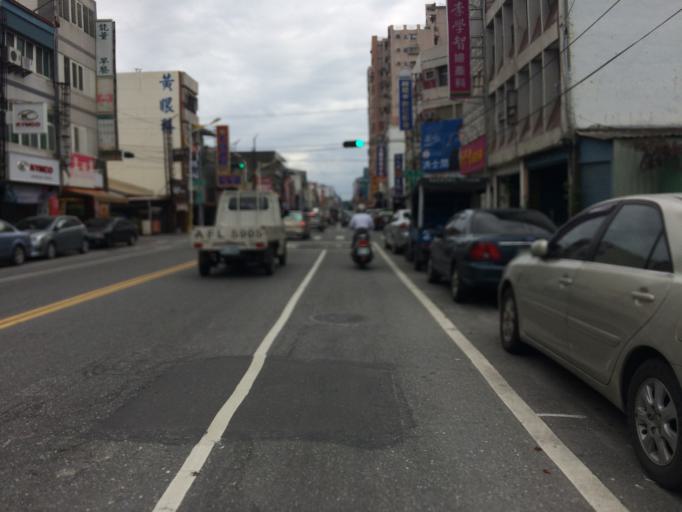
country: TW
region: Taiwan
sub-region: Hualien
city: Hualian
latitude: 23.9722
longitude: 121.5996
